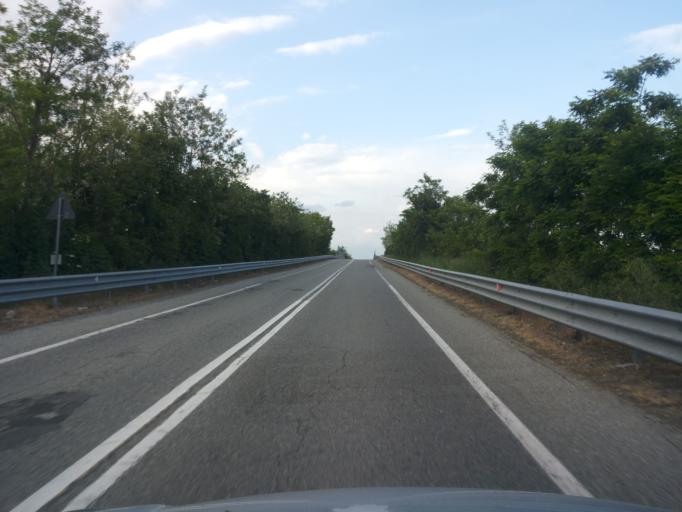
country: IT
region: Piedmont
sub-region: Provincia di Vercelli
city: Alice Castello
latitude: 45.3762
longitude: 8.0800
